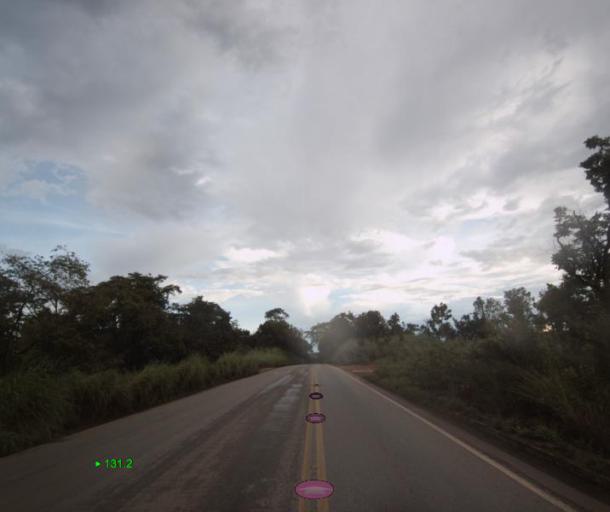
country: BR
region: Goias
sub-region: Porangatu
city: Porangatu
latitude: -13.9233
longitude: -49.0697
